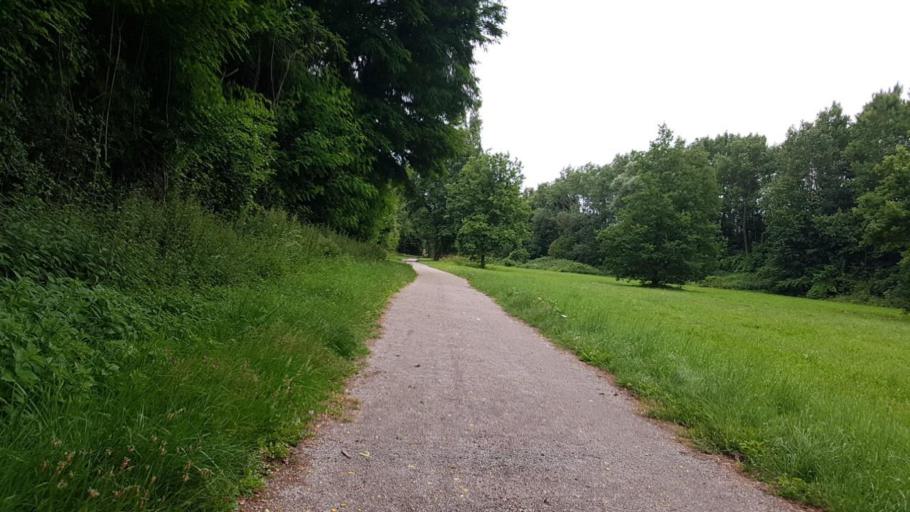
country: FR
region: Picardie
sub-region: Departement de l'Aisne
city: Origny-en-Thierache
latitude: 49.9296
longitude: 4.0271
